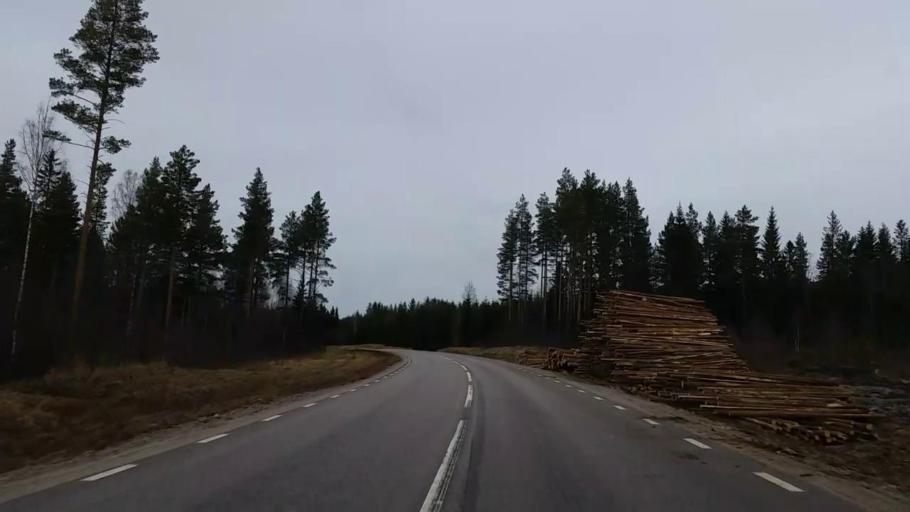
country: SE
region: Gaevleborg
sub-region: Ovanakers Kommun
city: Edsbyn
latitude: 61.1744
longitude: 15.8844
